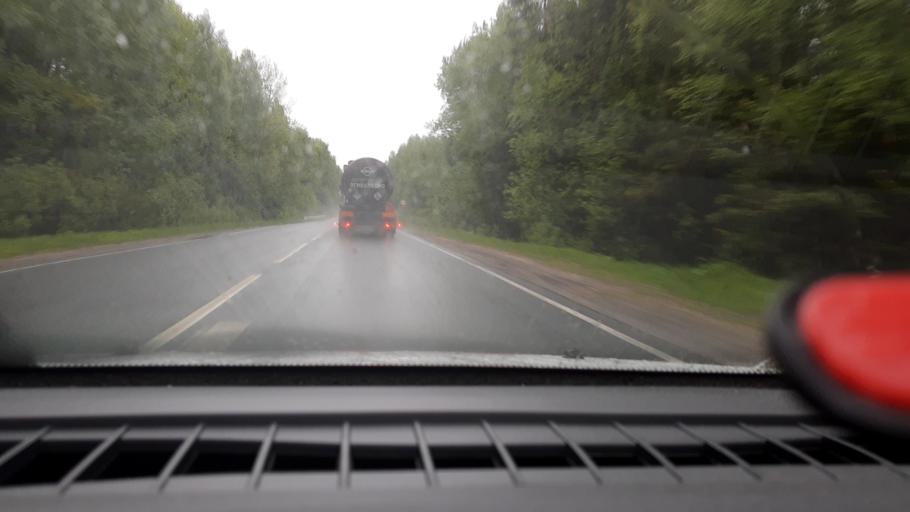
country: RU
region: Nizjnij Novgorod
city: Vladimirskoye
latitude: 56.8756
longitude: 44.9581
